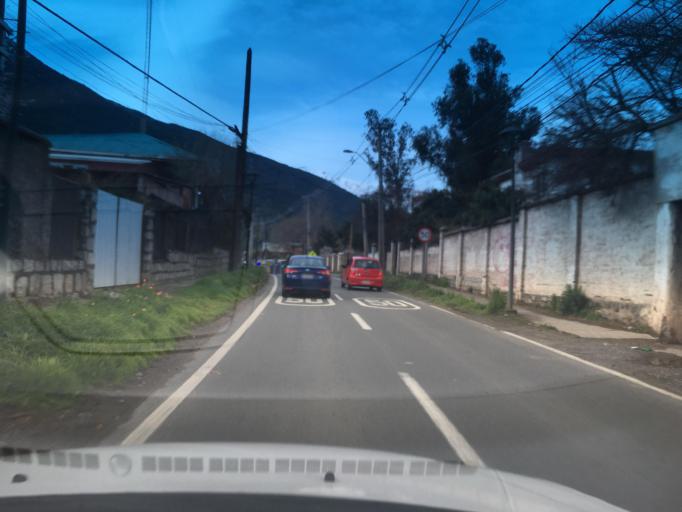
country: CL
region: Santiago Metropolitan
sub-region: Provincia de Cordillera
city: Puente Alto
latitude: -33.5918
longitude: -70.4856
